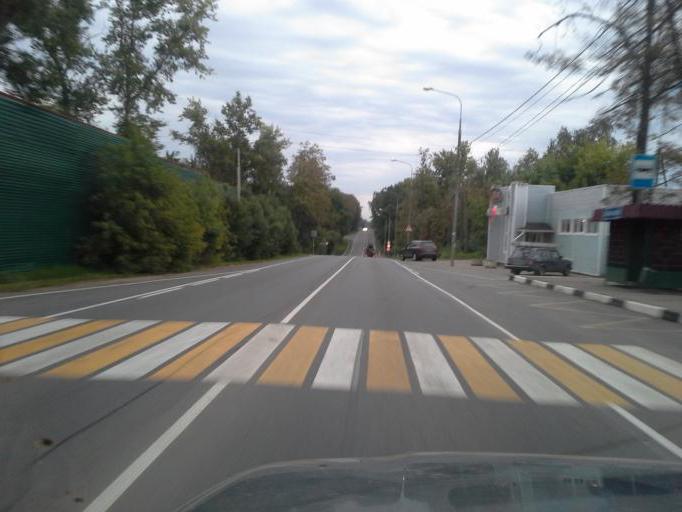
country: RU
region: Moskovskaya
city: Nazar'yevo
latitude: 55.6863
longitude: 37.0735
